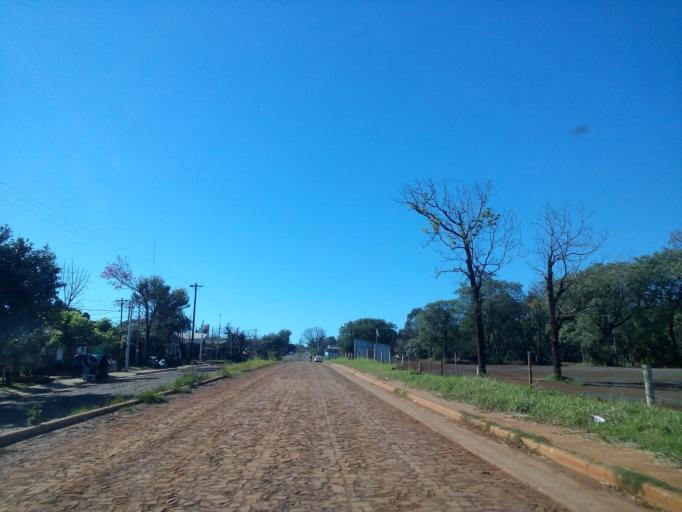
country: AR
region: Misiones
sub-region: Departamento de Capital
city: Posadas
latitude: -27.3920
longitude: -55.9230
